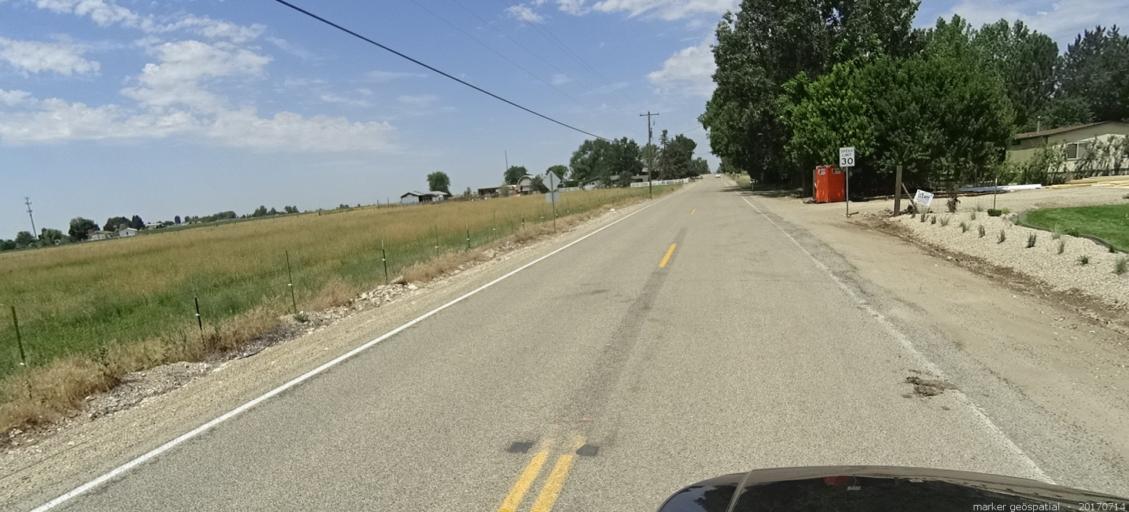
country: US
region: Idaho
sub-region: Ada County
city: Kuna
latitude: 43.5253
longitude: -116.3543
